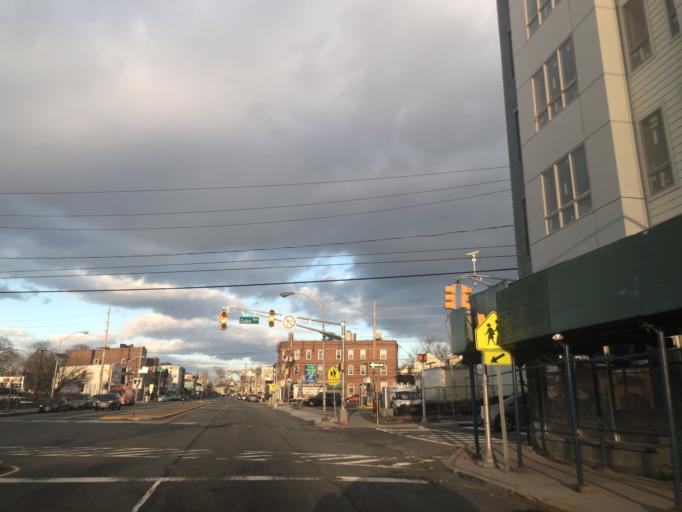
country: US
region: New Jersey
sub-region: Hudson County
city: Bayonne
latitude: 40.6946
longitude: -74.0999
